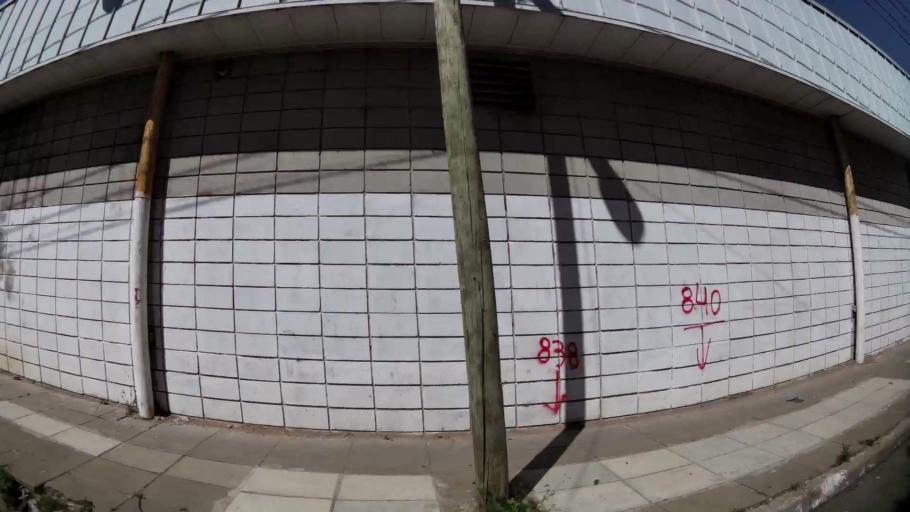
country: AR
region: Buenos Aires
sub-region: Partido de Quilmes
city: Quilmes
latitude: -34.7140
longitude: -58.2979
